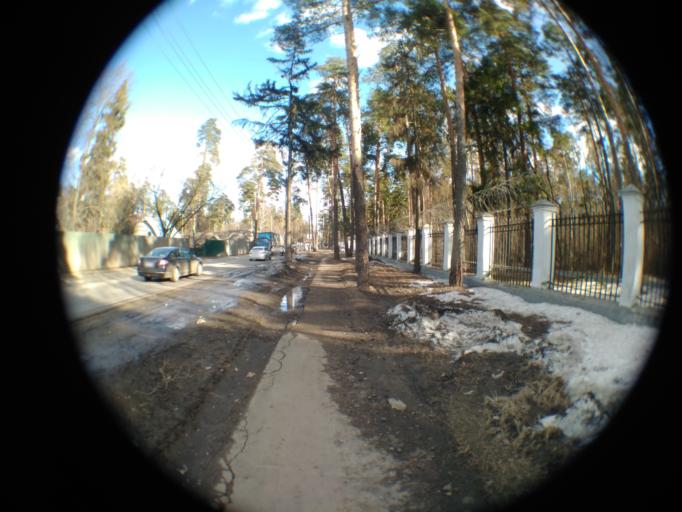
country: RU
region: Moskovskaya
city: Kratovo
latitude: 55.5800
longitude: 38.1524
